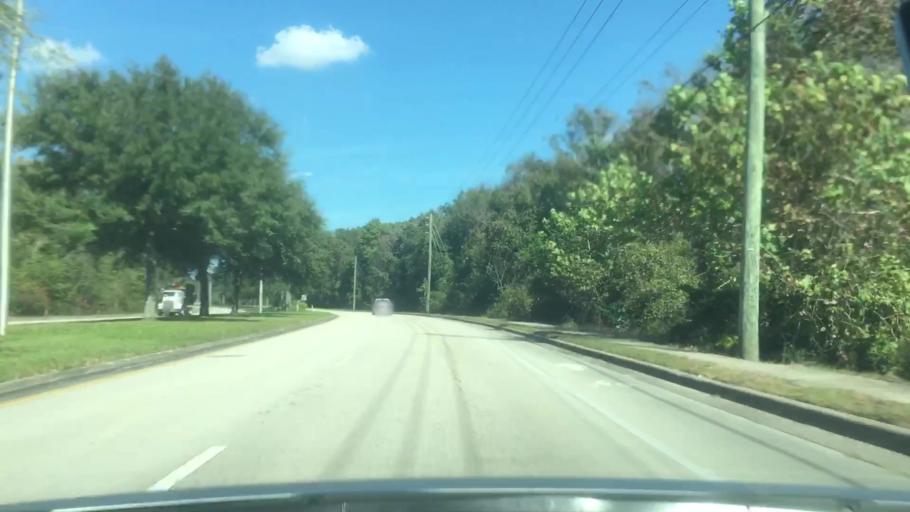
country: US
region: Florida
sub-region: Duval County
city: Atlantic Beach
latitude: 30.3546
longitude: -81.5061
